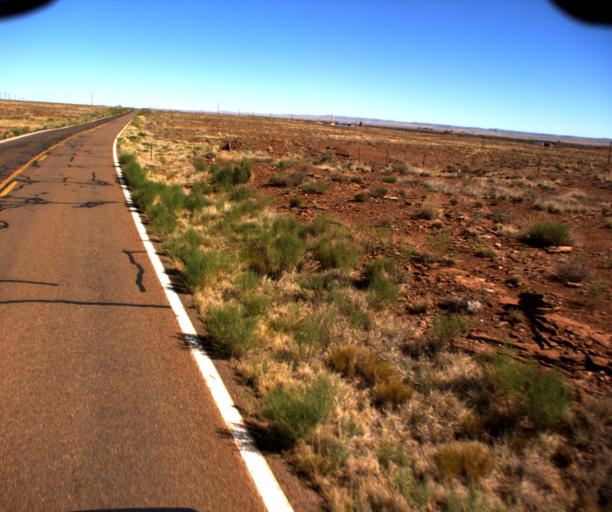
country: US
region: Arizona
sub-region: Coconino County
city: LeChee
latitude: 35.2800
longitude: -110.9817
